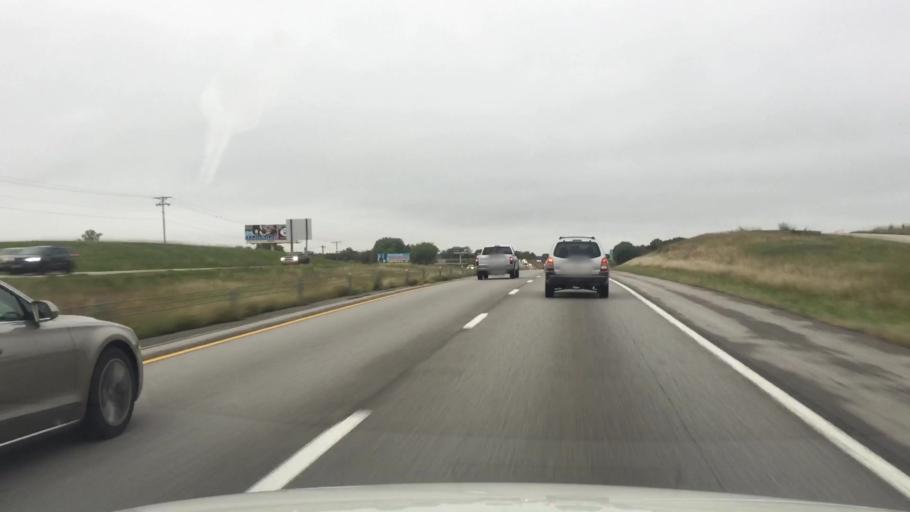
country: US
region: Missouri
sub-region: Jackson County
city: Oak Grove
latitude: 39.0168
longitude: -94.1424
